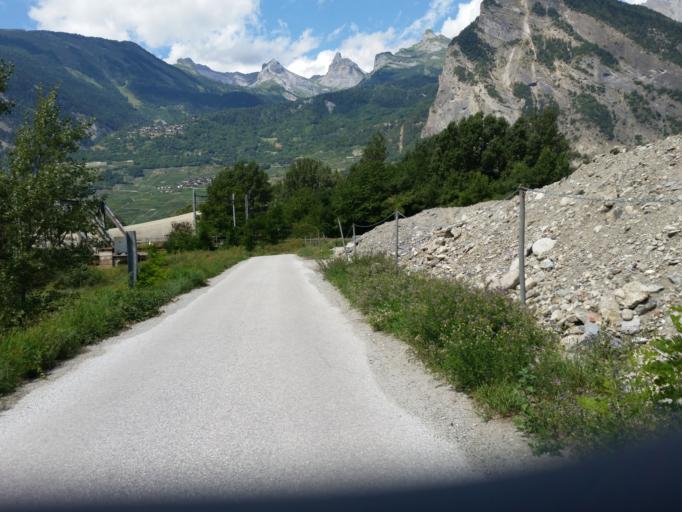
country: CH
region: Valais
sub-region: Martigny District
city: Riddes
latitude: 46.1781
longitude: 7.2268
